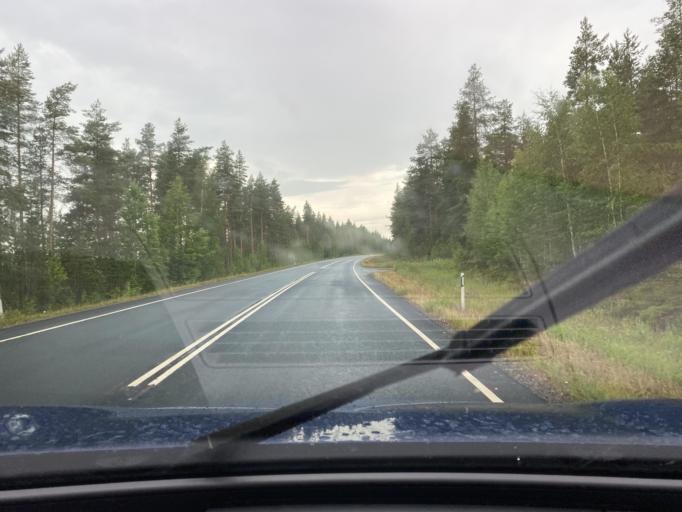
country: FI
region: Central Ostrobothnia
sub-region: Kaustinen
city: Veteli
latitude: 63.4113
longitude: 23.9578
